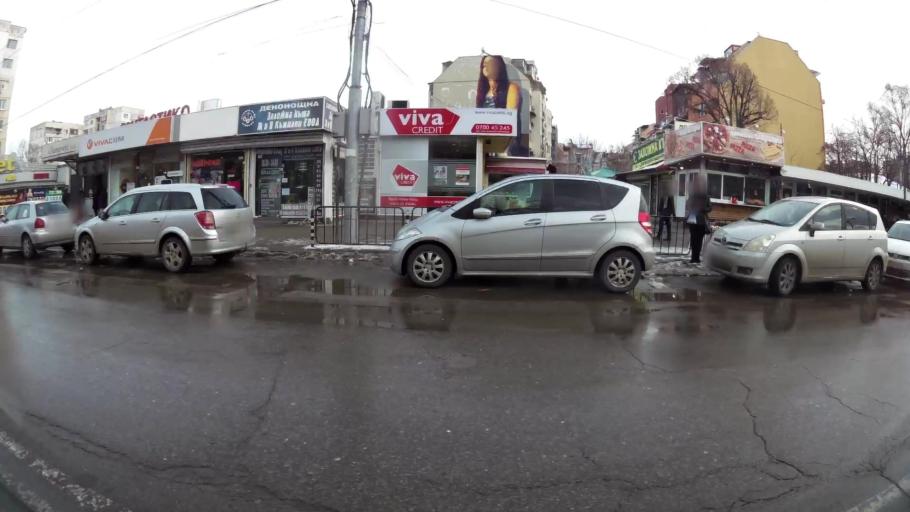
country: BG
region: Sofia-Capital
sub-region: Stolichna Obshtina
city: Sofia
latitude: 42.7068
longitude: 23.3507
